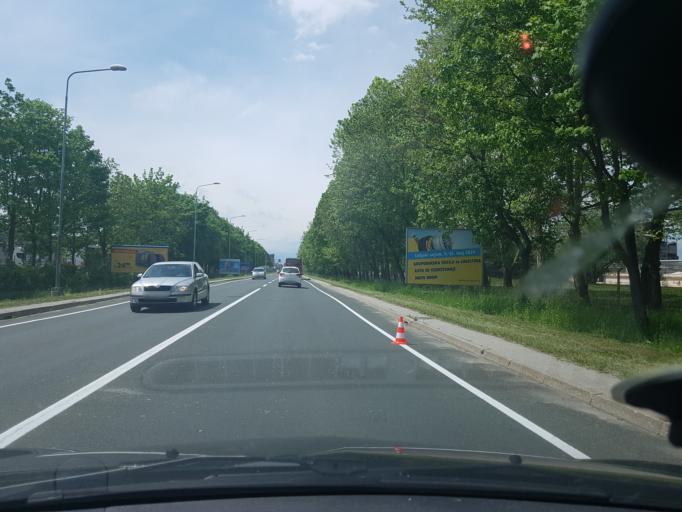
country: SI
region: Celje
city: Trnovlje pri Celju
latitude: 46.2345
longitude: 15.2941
